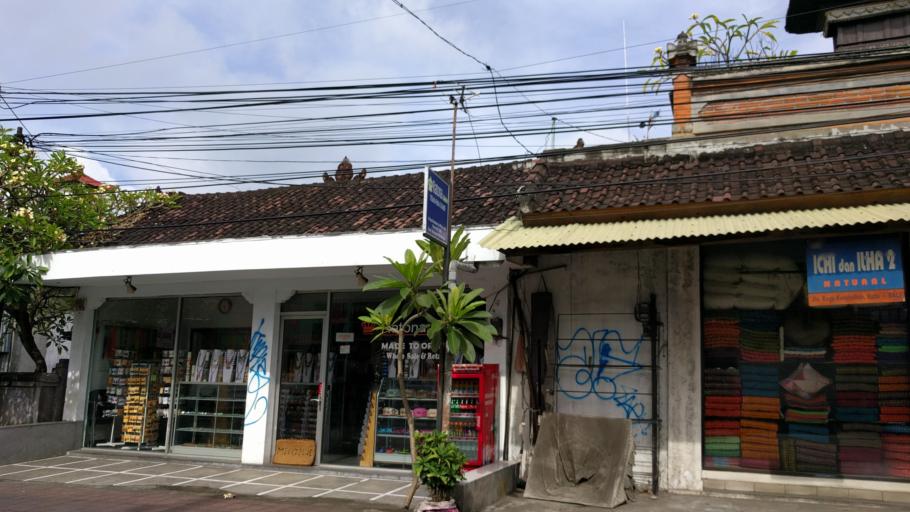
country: ID
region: Bali
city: Kuta
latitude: -8.6787
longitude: 115.1646
